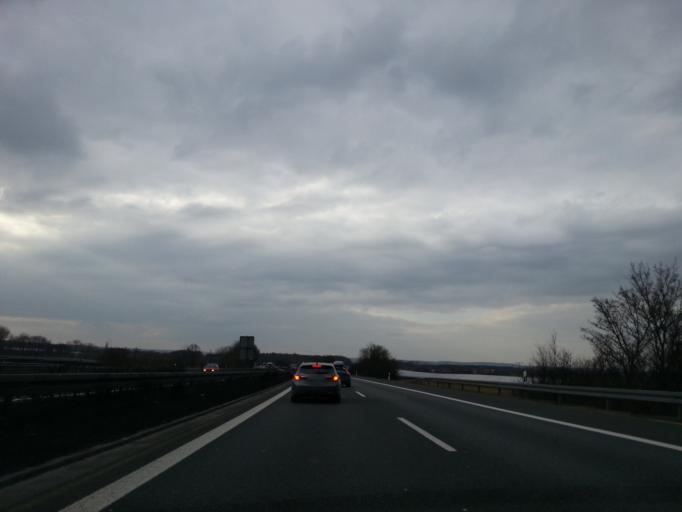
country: DE
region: Bavaria
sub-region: Regierungsbezirk Unterfranken
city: Kleinlangheim
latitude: 49.7808
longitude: 10.2948
